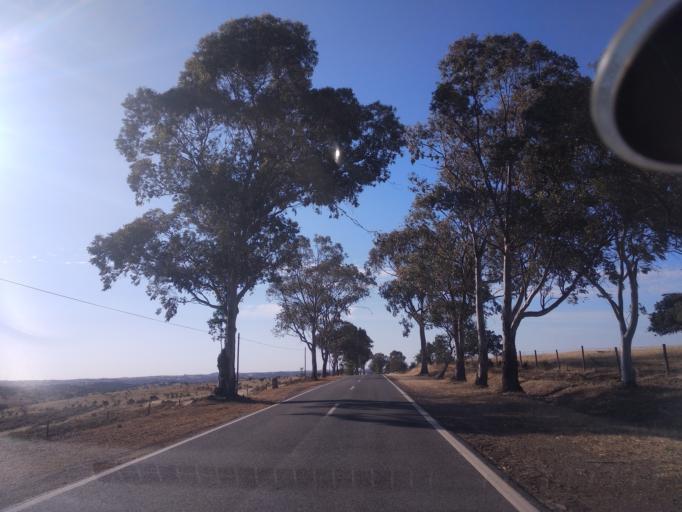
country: PT
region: Beja
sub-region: Almodovar
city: Almodovar
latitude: 37.4546
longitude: -7.9977
